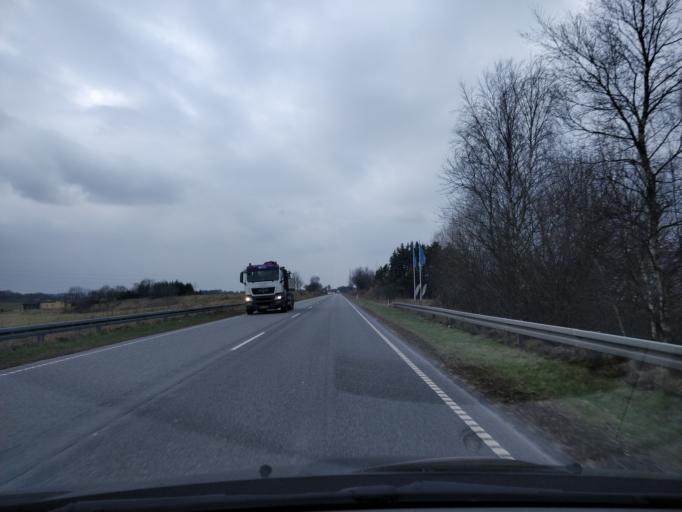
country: DK
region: South Denmark
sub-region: Vejle Kommune
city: Brejning
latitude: 55.6270
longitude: 9.7185
